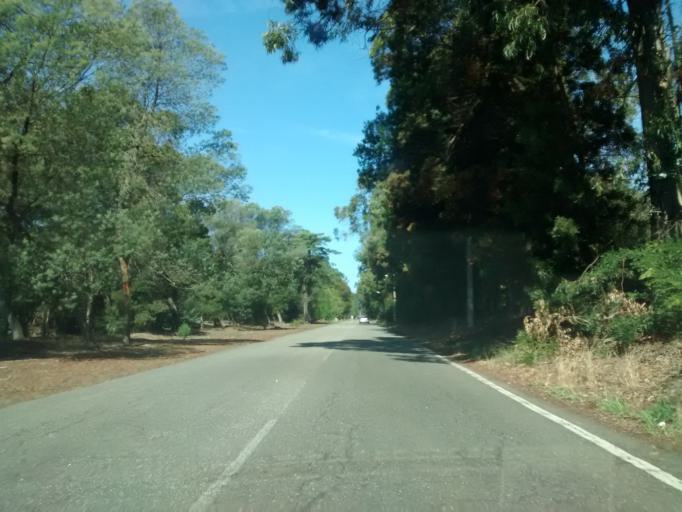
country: PT
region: Coimbra
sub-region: Mira
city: Mira
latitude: 40.4496
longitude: -8.7676
